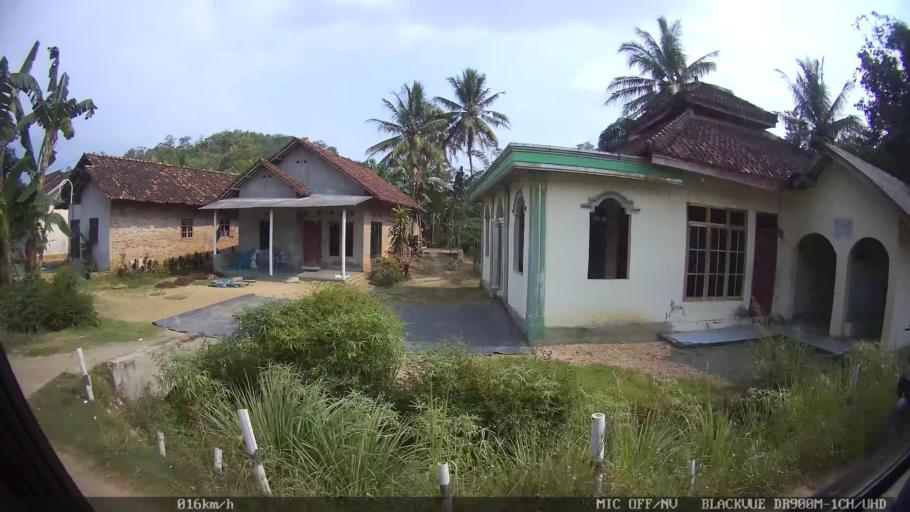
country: ID
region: Lampung
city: Kedondong
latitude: -5.4106
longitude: 105.0113
